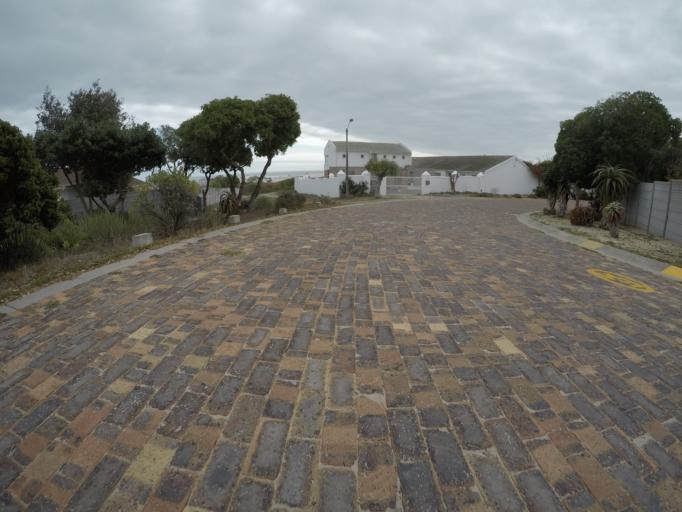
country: ZA
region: Western Cape
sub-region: City of Cape Town
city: Atlantis
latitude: -33.6936
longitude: 18.4406
